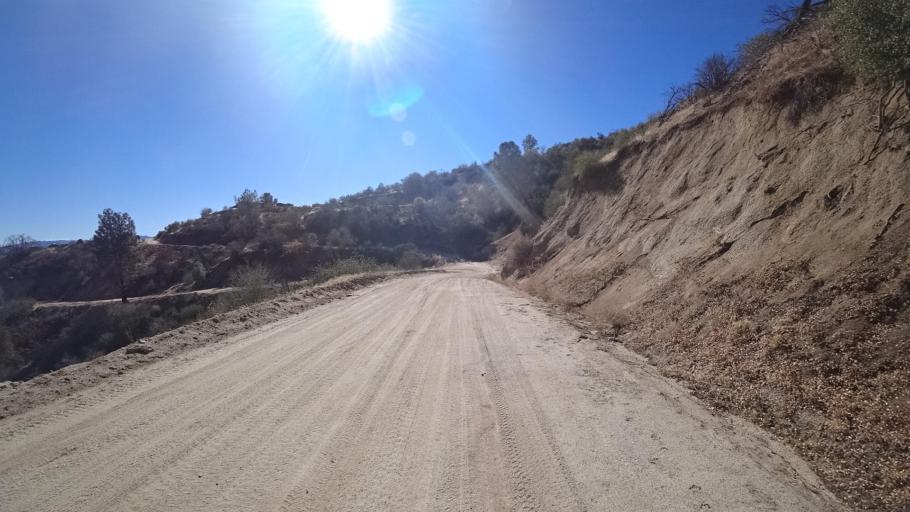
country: US
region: California
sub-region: Kern County
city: Alta Sierra
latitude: 35.7102
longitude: -118.5088
